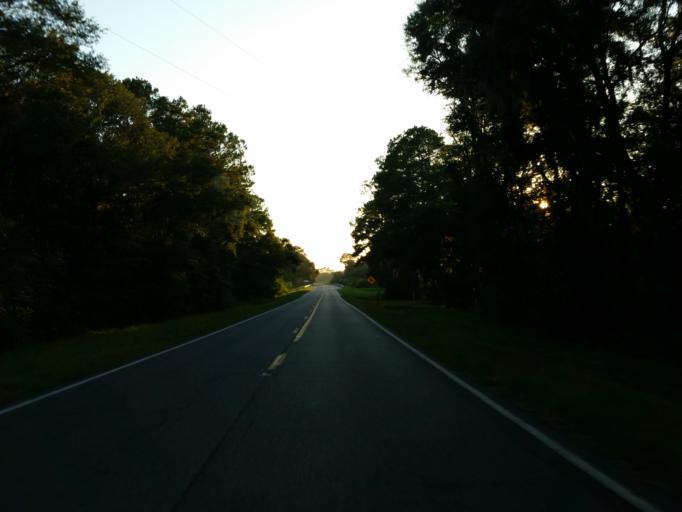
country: US
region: Georgia
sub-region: Berrien County
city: Nashville
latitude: 31.1862
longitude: -83.1756
